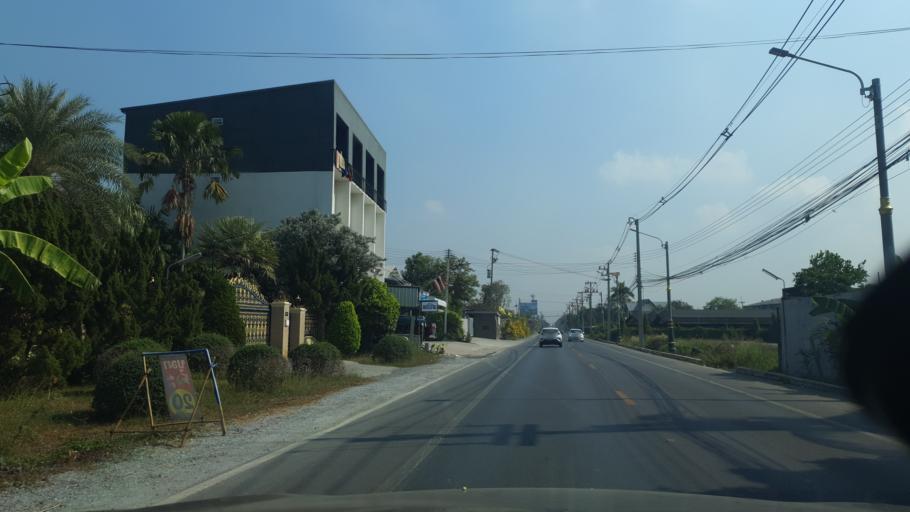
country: TH
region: Nakhon Pathom
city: Salaya
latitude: 13.7723
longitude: 100.2899
